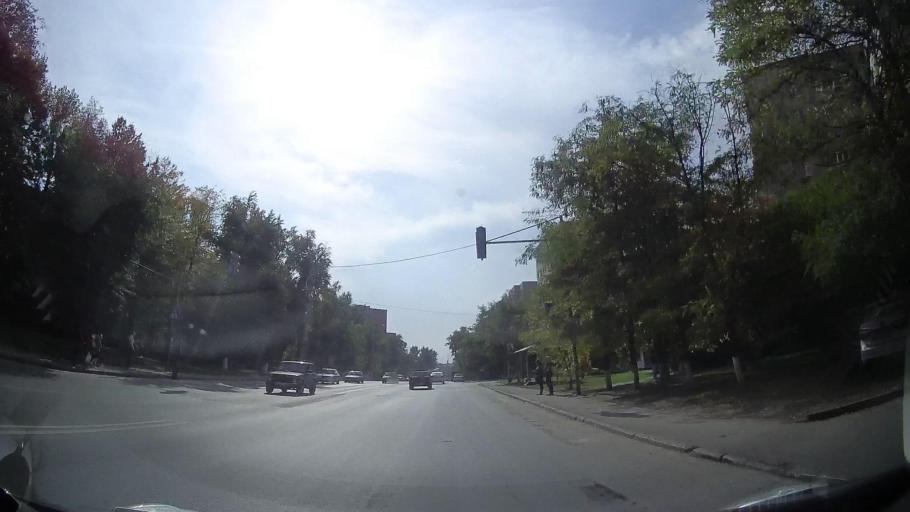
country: RU
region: Rostov
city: Severnyy
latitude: 47.2815
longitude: 39.7078
